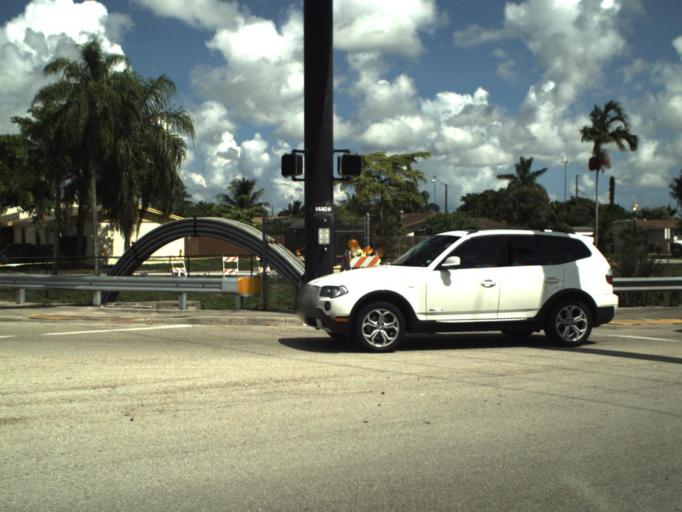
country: US
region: Florida
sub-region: Broward County
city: Miramar
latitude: 25.9946
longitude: -80.2476
